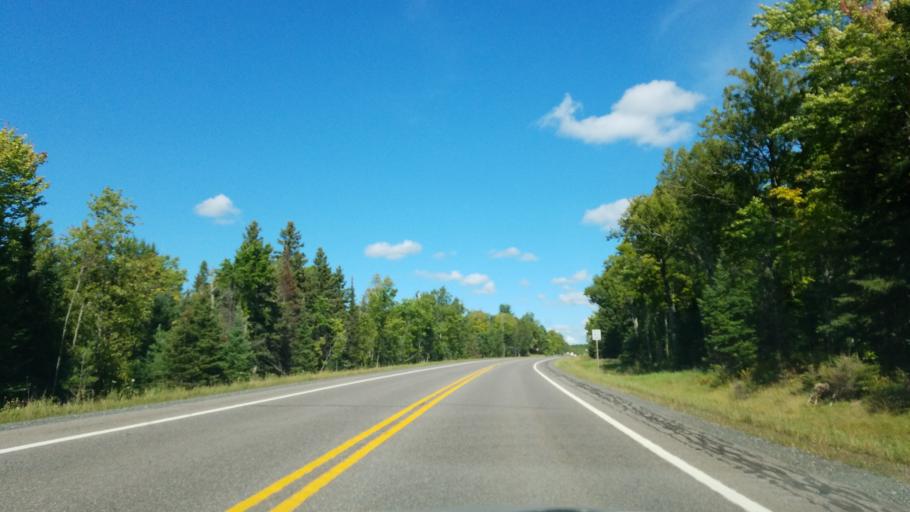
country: US
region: Michigan
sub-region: Baraga County
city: L'Anse
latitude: 46.5799
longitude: -88.4853
